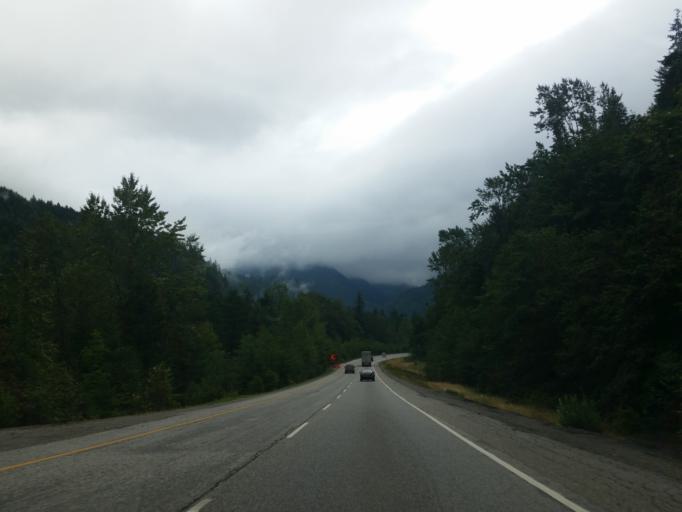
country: CA
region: British Columbia
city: Hope
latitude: 49.3787
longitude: -121.3579
